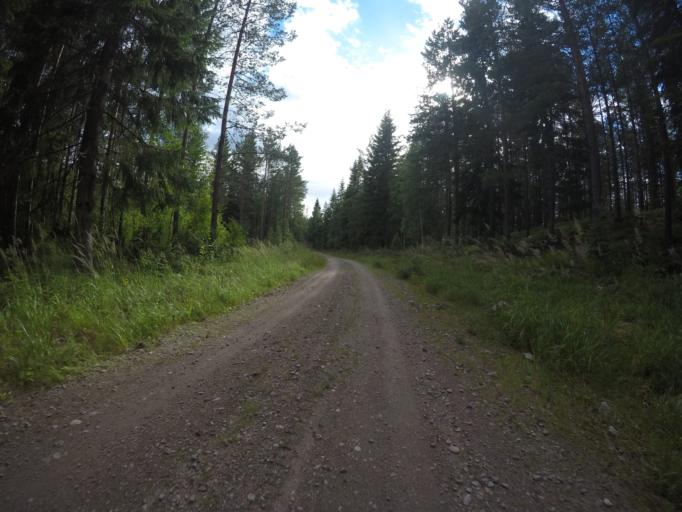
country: SE
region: Vaermland
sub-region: Filipstads Kommun
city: Lesjofors
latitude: 60.0428
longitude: 14.3737
